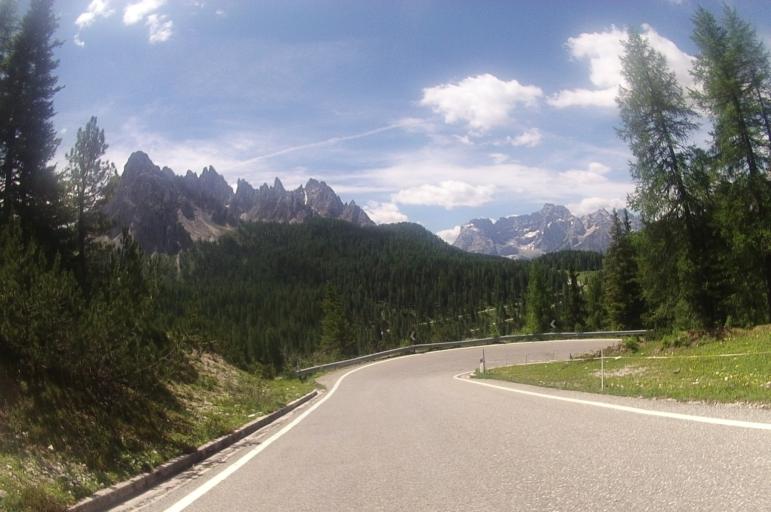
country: IT
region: Trentino-Alto Adige
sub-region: Bolzano
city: Sesto
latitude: 46.6071
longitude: 12.2757
